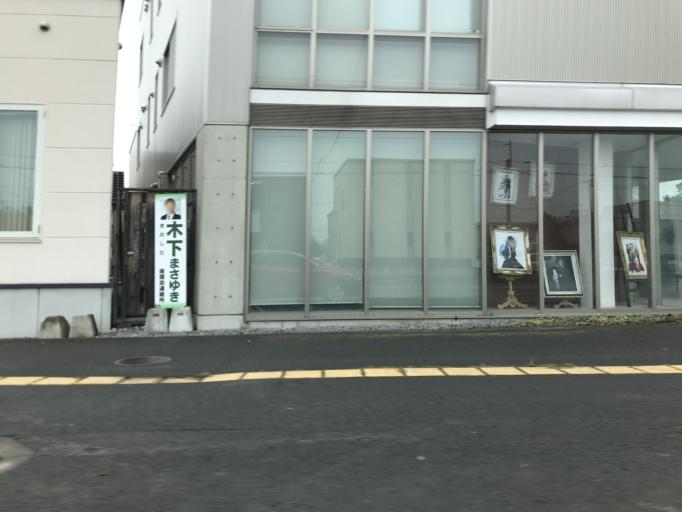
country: JP
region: Hokkaido
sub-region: Asahikawa-shi
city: Asahikawa
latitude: 43.7626
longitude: 142.3464
